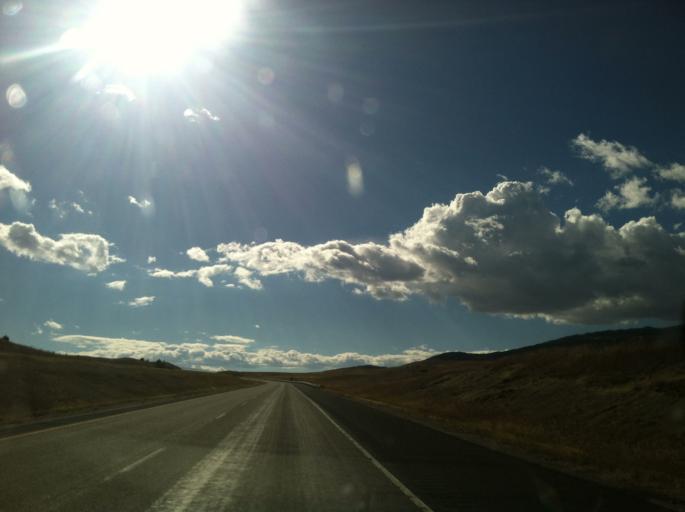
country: US
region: Montana
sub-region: Jefferson County
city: Whitehall
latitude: 45.8941
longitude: -111.8461
